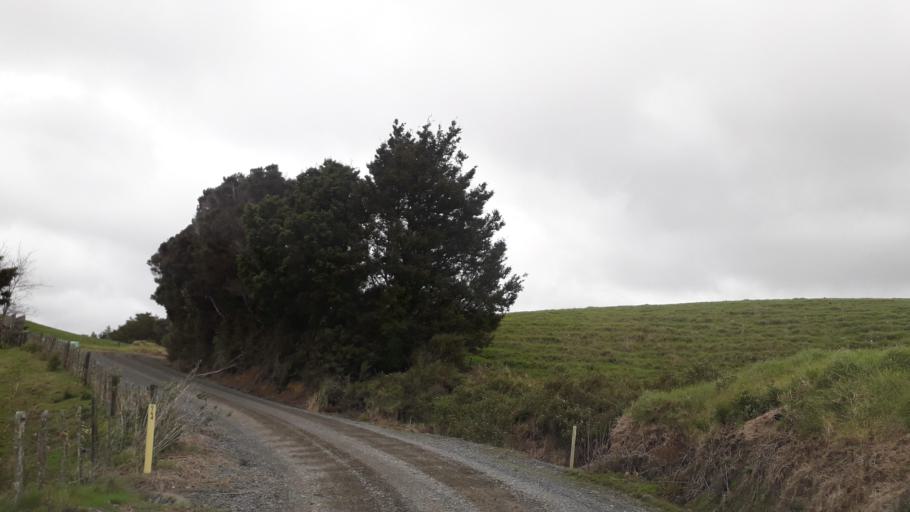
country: NZ
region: Northland
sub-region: Far North District
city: Waimate North
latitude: -35.1399
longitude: 173.7129
